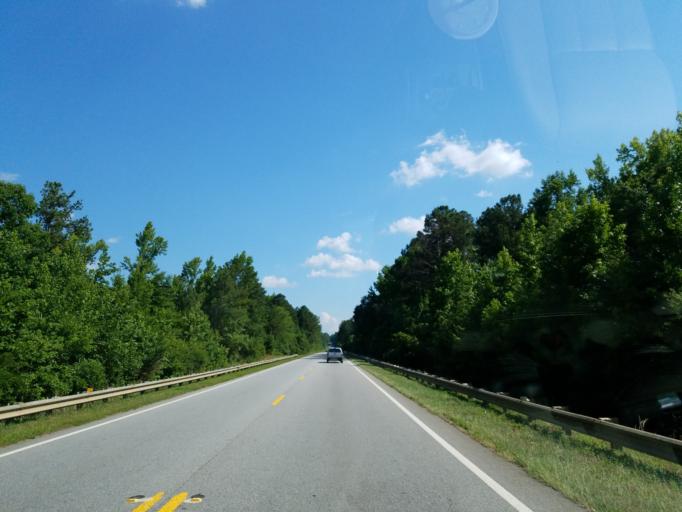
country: US
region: Georgia
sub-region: Crawford County
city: Roberta
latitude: 32.7790
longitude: -84.0219
